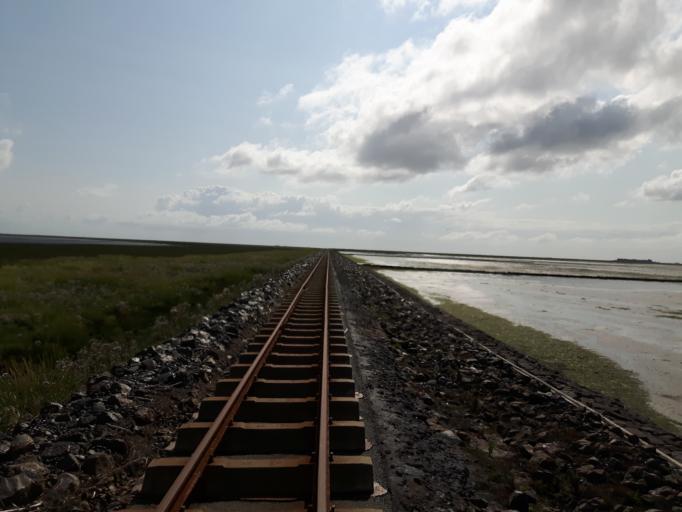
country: DE
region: Schleswig-Holstein
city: Dagebull
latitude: 54.6970
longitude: 8.7106
